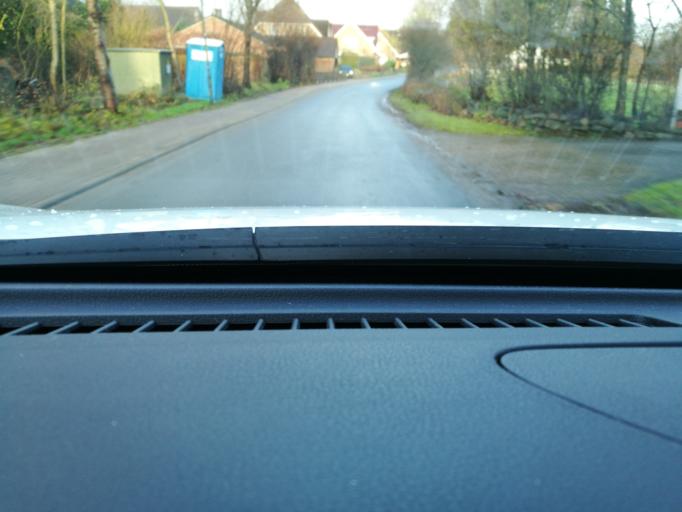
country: DE
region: Schleswig-Holstein
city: Ascheffel
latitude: 54.4274
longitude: 9.6995
